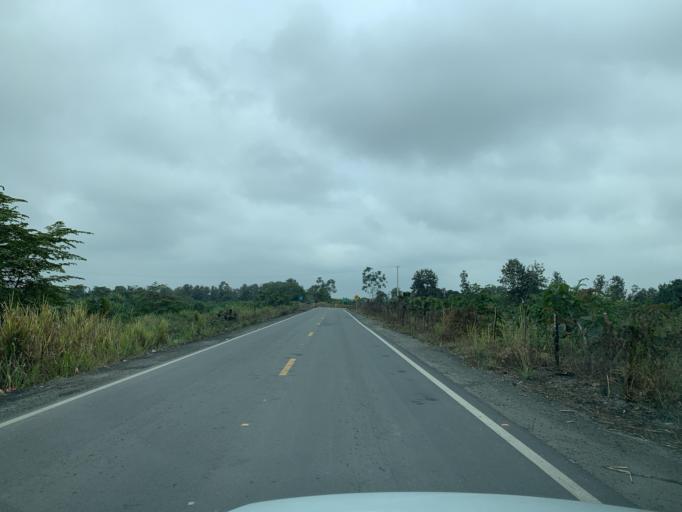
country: EC
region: Guayas
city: Coronel Marcelino Mariduena
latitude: -2.2977
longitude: -79.5039
